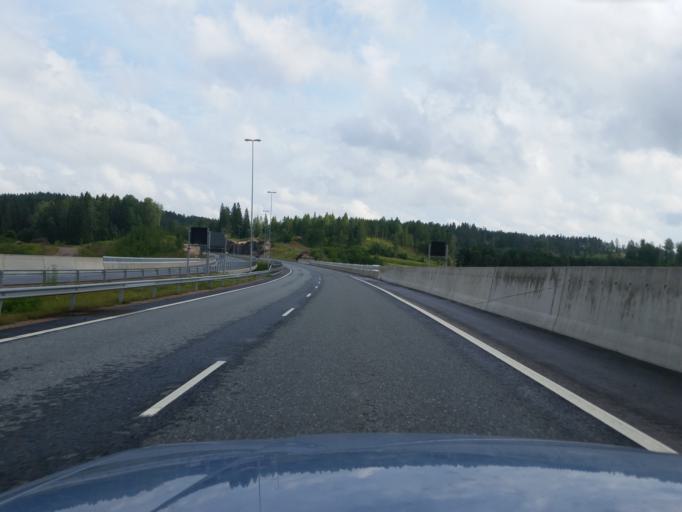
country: FI
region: Uusimaa
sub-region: Helsinki
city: Saukkola
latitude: 60.3311
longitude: 23.9318
